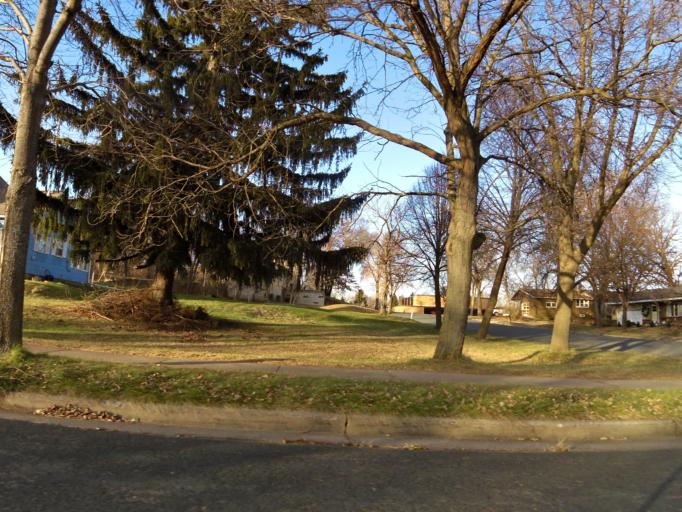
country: US
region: Wisconsin
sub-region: Pierce County
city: River Falls
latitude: 44.8617
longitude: -92.6366
